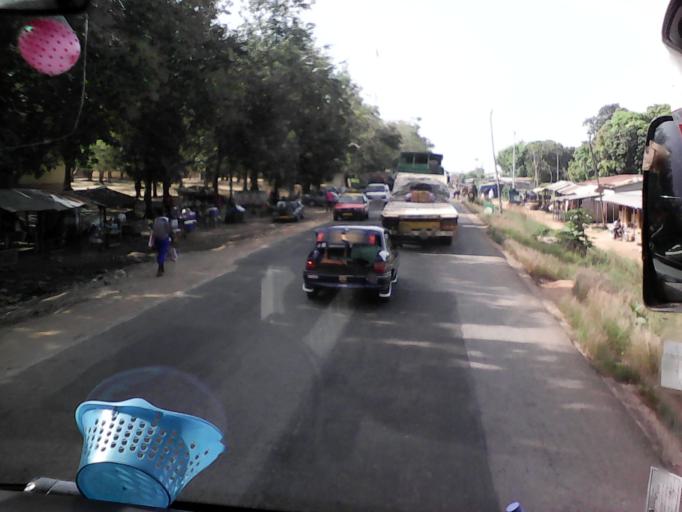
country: TG
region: Centrale
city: Sokode
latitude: 9.0199
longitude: 1.1407
